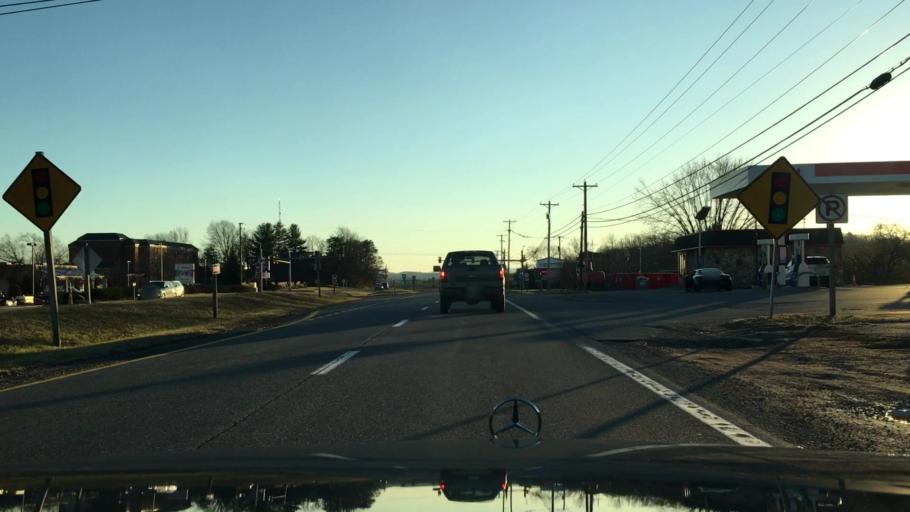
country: US
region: Virginia
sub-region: Montgomery County
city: Merrimac
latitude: 37.1870
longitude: -80.4078
